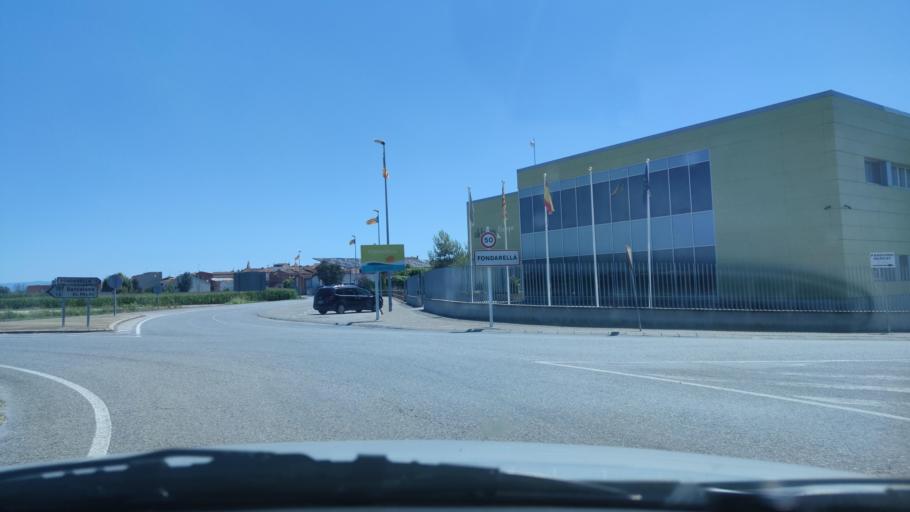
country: ES
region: Catalonia
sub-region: Provincia de Lleida
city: Mollerussa
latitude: 41.6382
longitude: 0.8749
